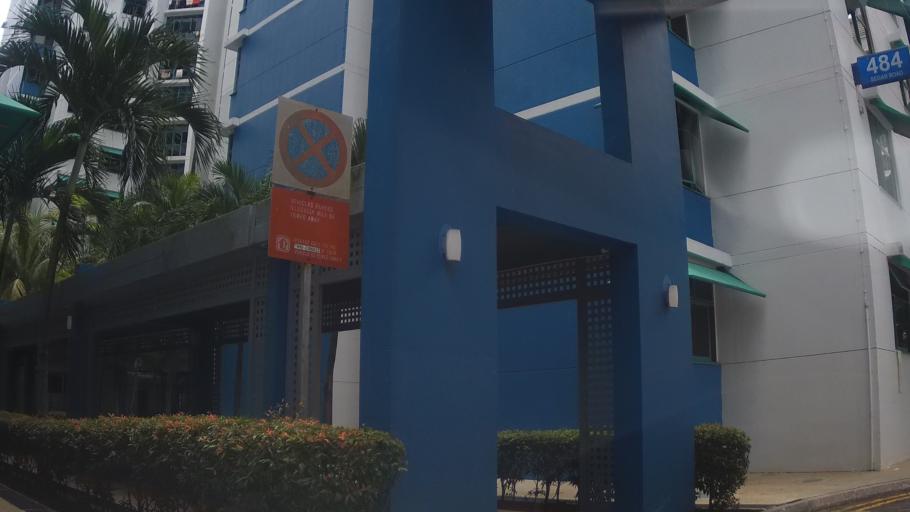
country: MY
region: Johor
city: Johor Bahru
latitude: 1.3888
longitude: 103.7719
